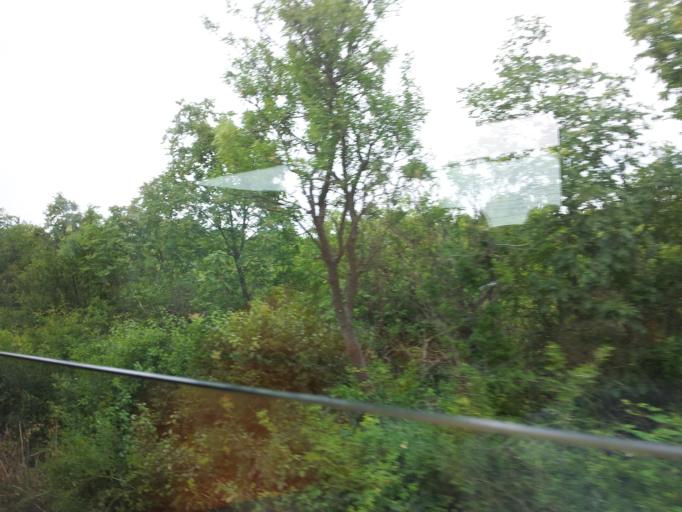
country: HU
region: Veszprem
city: Zanka
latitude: 46.8773
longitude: 17.7037
